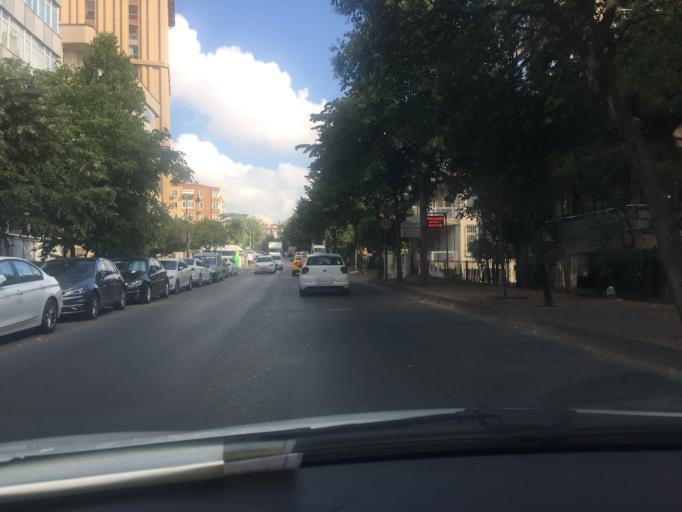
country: TR
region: Istanbul
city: Sisli
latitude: 41.0626
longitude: 28.9977
